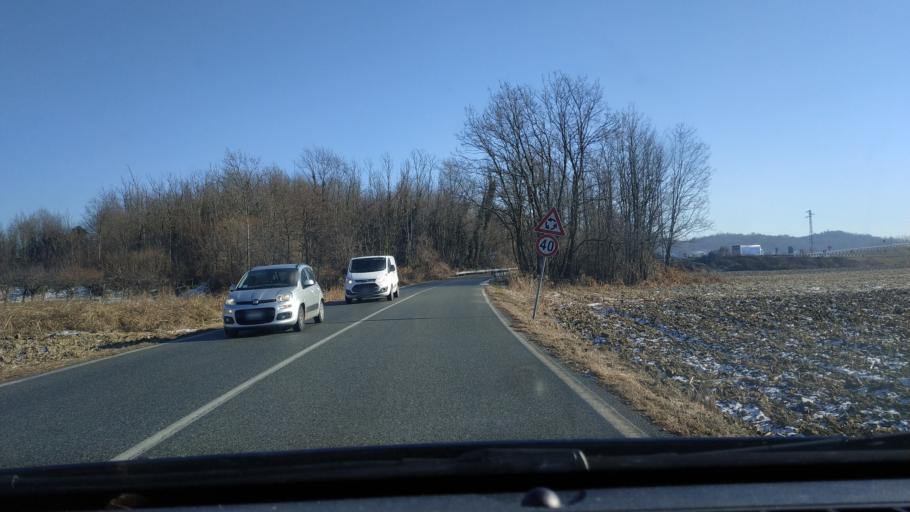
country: IT
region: Piedmont
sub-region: Provincia di Torino
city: Samone
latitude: 45.4449
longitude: 7.8375
